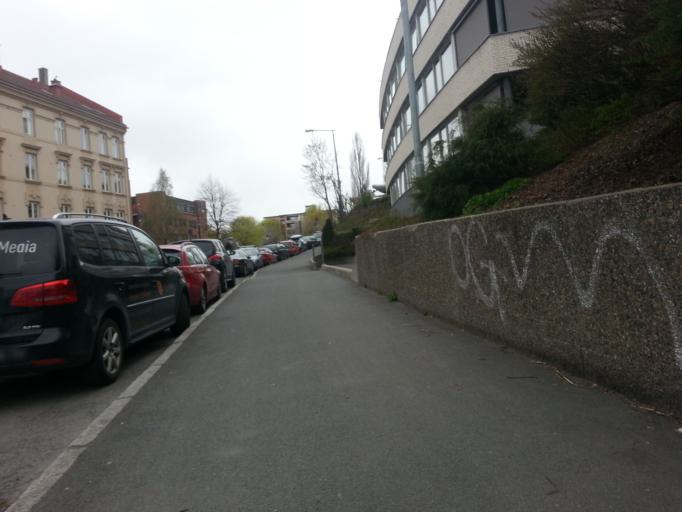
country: NO
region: Oslo
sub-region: Oslo
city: Sjolyststranda
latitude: 59.9239
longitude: 10.6812
